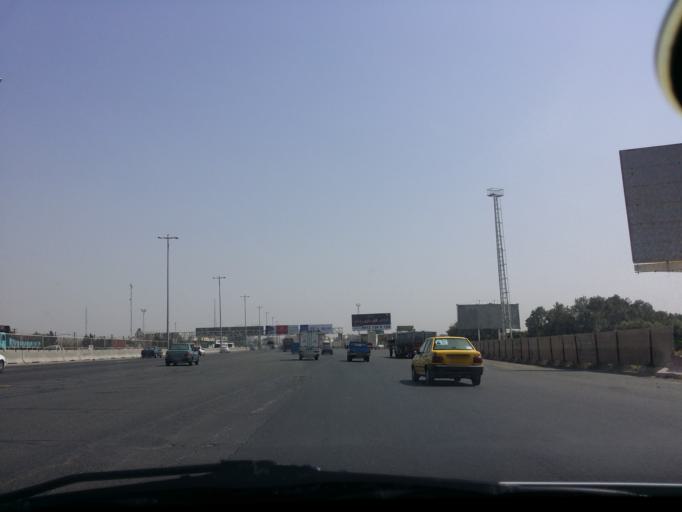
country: IR
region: Alborz
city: Karaj
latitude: 35.8388
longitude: 50.9096
